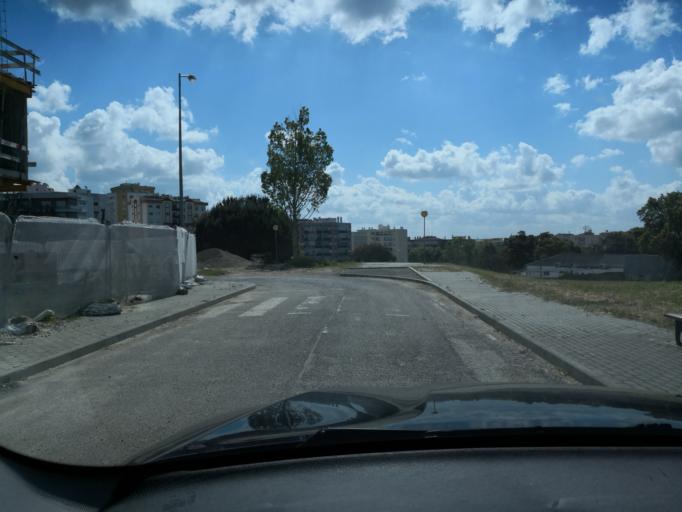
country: PT
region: Setubal
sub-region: Setubal
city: Setubal
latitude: 38.5340
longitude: -8.8726
